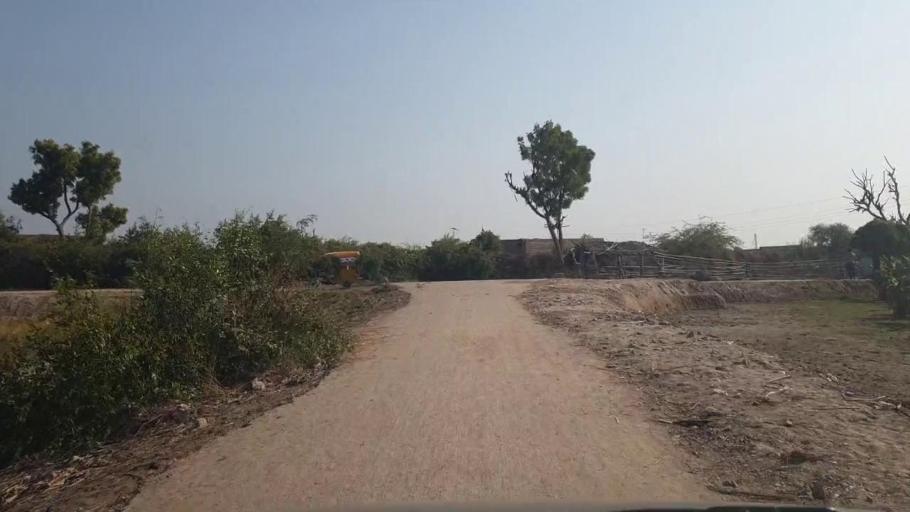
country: PK
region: Sindh
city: Bhit Shah
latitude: 25.8095
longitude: 68.5788
